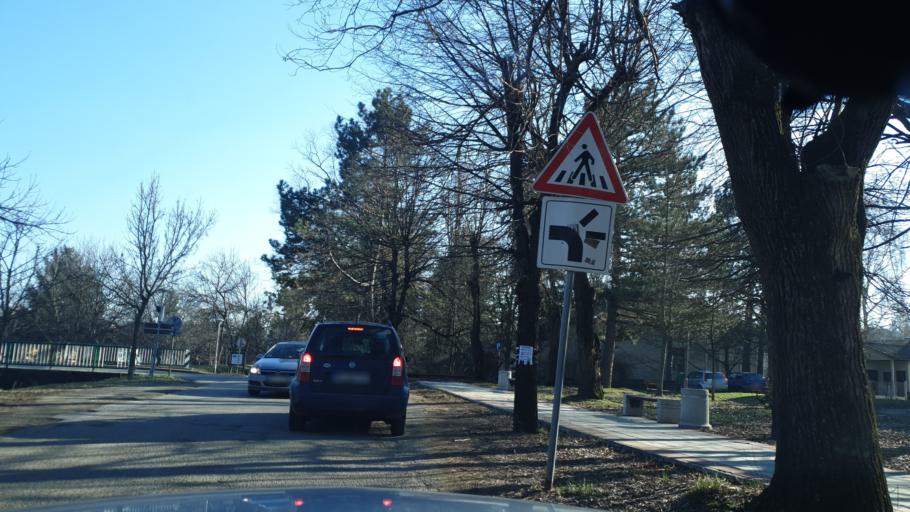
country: RS
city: Vrdnik
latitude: 45.1237
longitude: 19.7878
